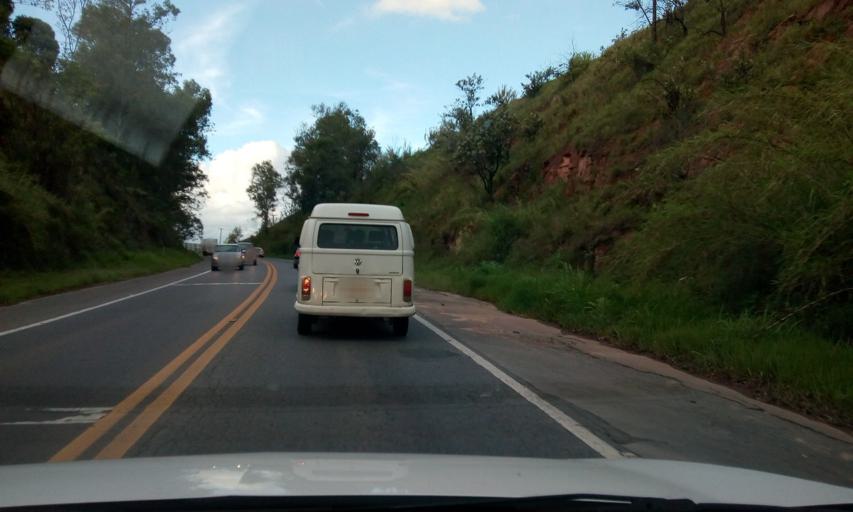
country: BR
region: Sao Paulo
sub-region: Itatiba
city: Itatiba
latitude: -23.0123
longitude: -46.8202
